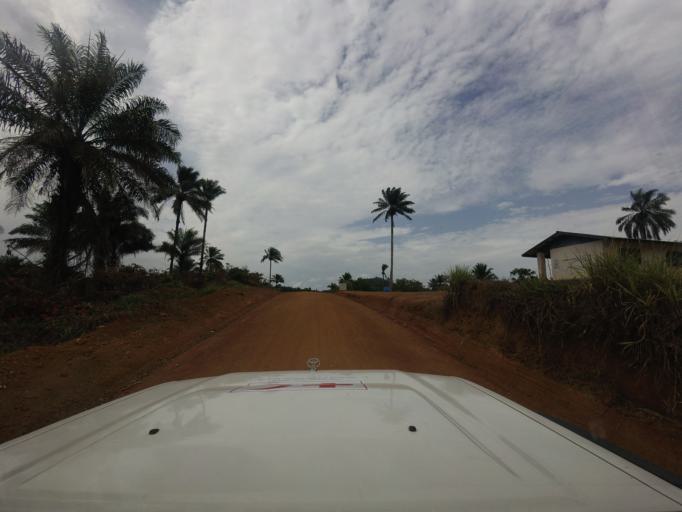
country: SL
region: Eastern Province
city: Buedu
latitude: 8.2365
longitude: -10.2220
